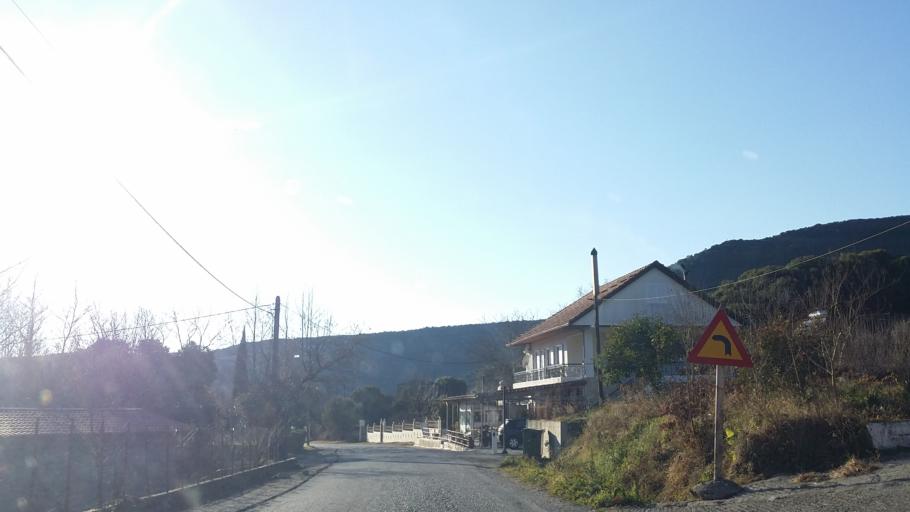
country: GR
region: West Greece
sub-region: Nomos Aitolias kai Akarnanias
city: Neapolis
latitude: 38.7683
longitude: 21.4459
